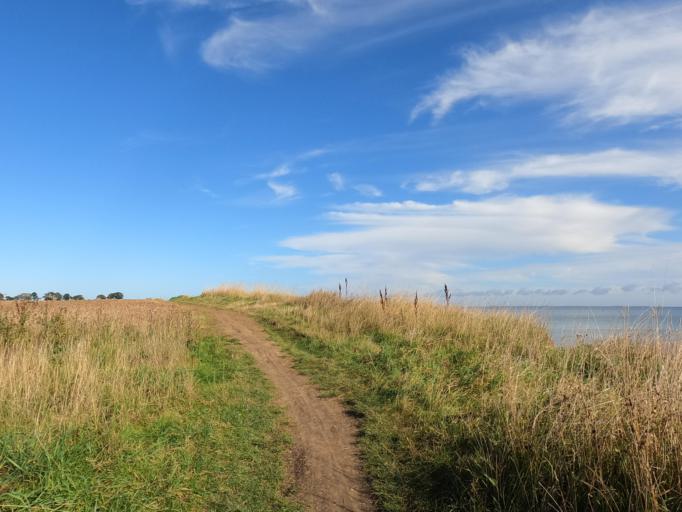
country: DE
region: Schleswig-Holstein
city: Dahme
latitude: 54.2823
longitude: 11.0825
